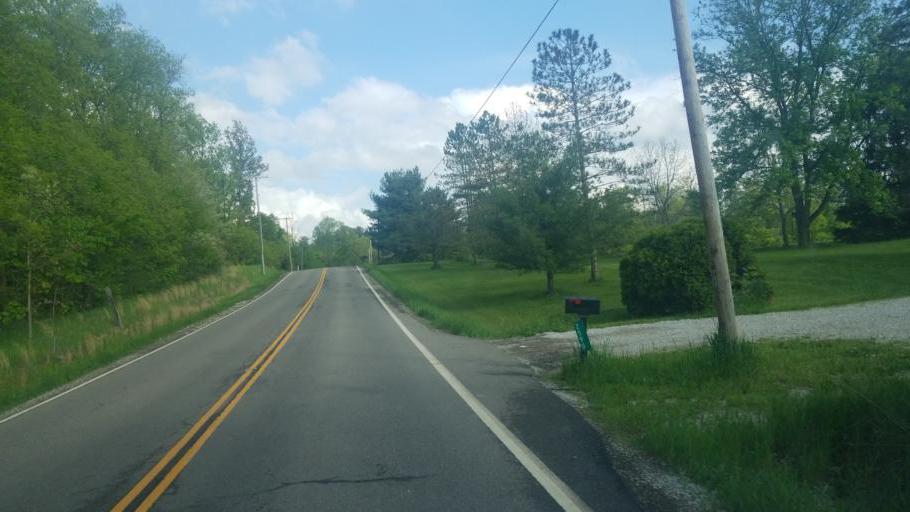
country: US
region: Ohio
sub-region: Ashland County
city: Ashland
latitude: 40.8808
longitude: -82.4192
